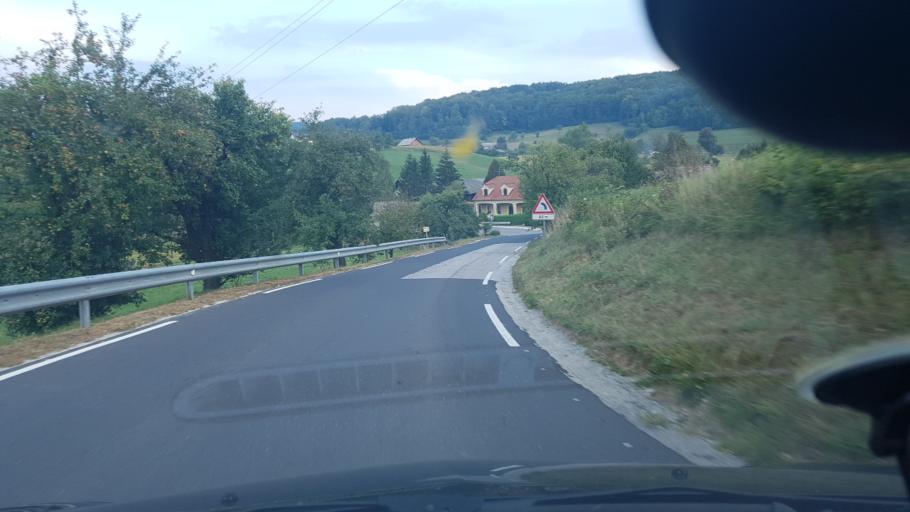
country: SI
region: Kozje
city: Kozje
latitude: 46.0344
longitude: 15.5333
